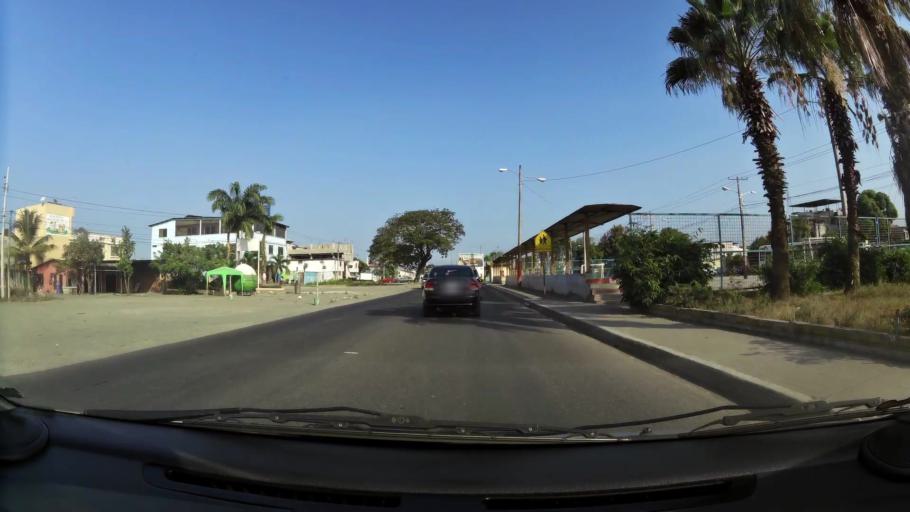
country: EC
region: Guayas
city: Eloy Alfaro
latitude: -2.1815
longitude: -79.8390
